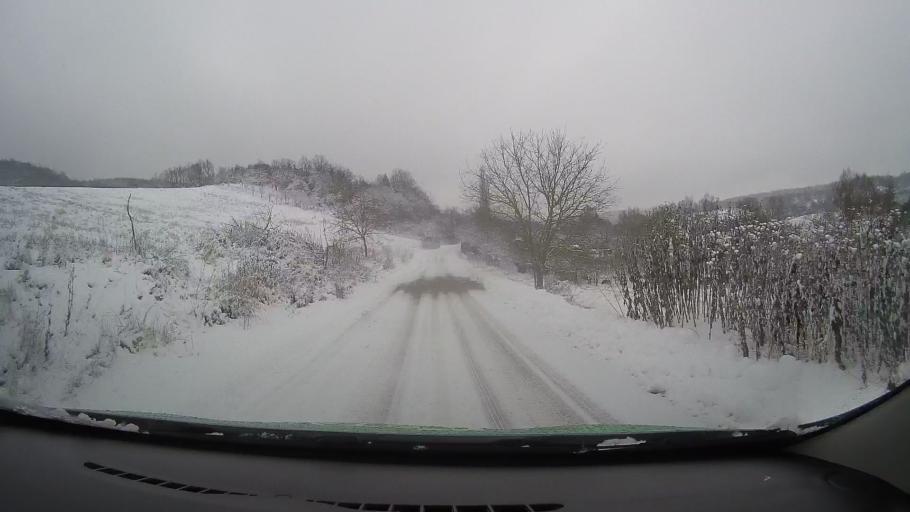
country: RO
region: Hunedoara
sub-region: Comuna Pestisu Mic
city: Pestisu Mic
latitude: 45.8243
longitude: 22.8599
